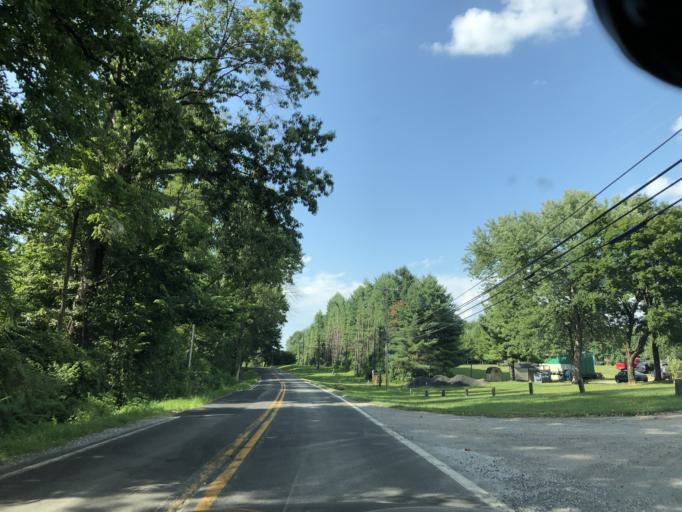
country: US
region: Maryland
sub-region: Frederick County
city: Linganore
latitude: 39.4157
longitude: -77.1752
